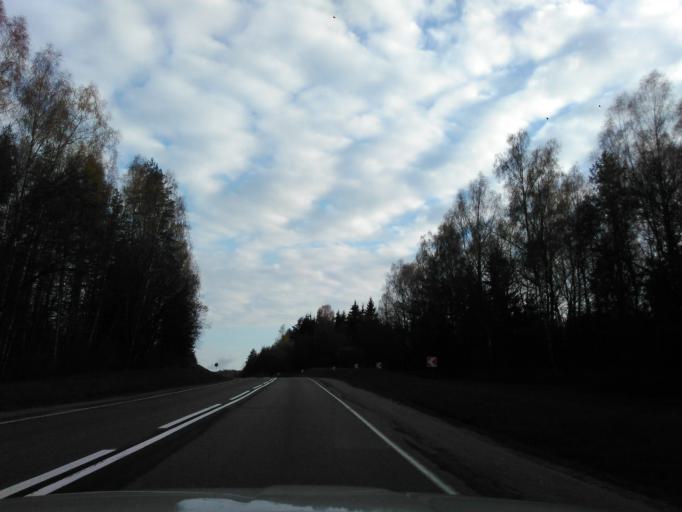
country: BY
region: Minsk
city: Plyeshchanitsy
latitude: 54.3337
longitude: 27.8758
